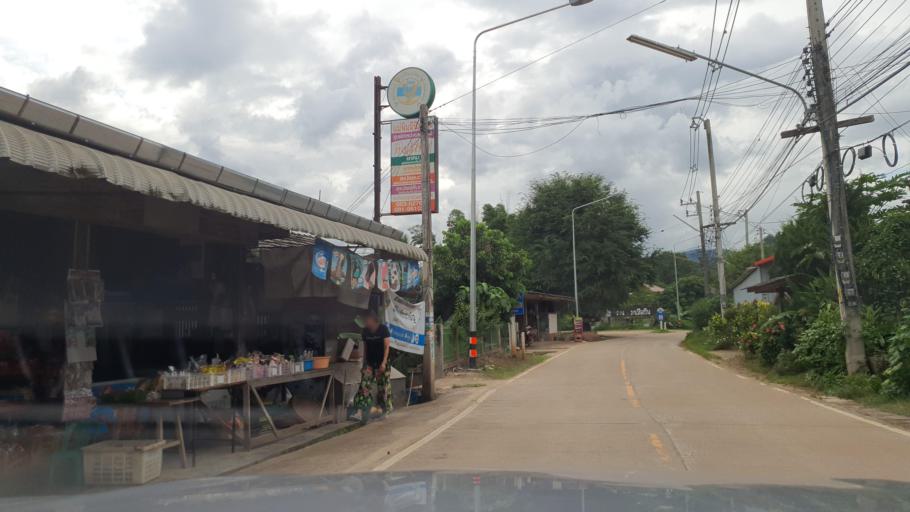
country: TH
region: Chiang Mai
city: Mae Wang
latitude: 18.6614
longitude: 98.6621
